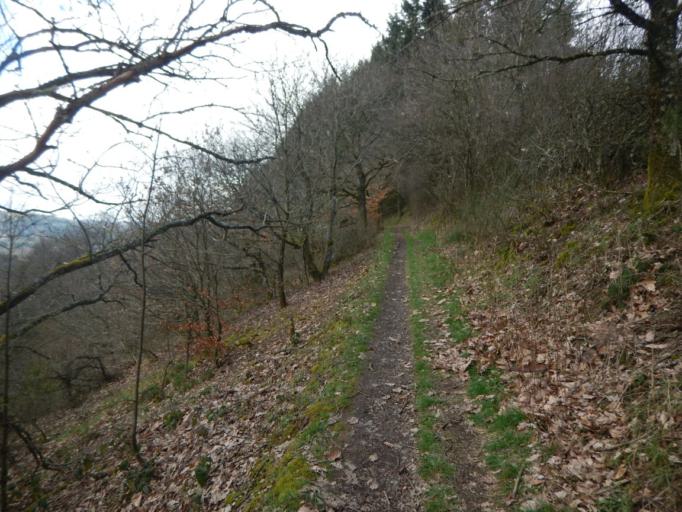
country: LU
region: Diekirch
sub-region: Canton de Wiltz
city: Esch-sur-Sure
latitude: 49.9162
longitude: 5.9038
